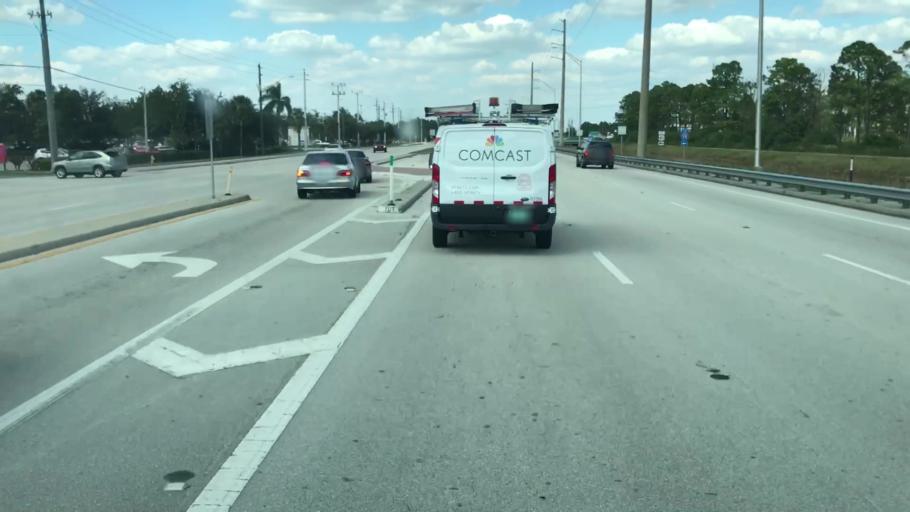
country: US
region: Florida
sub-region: Collier County
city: Vineyards
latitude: 26.2697
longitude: -81.6893
